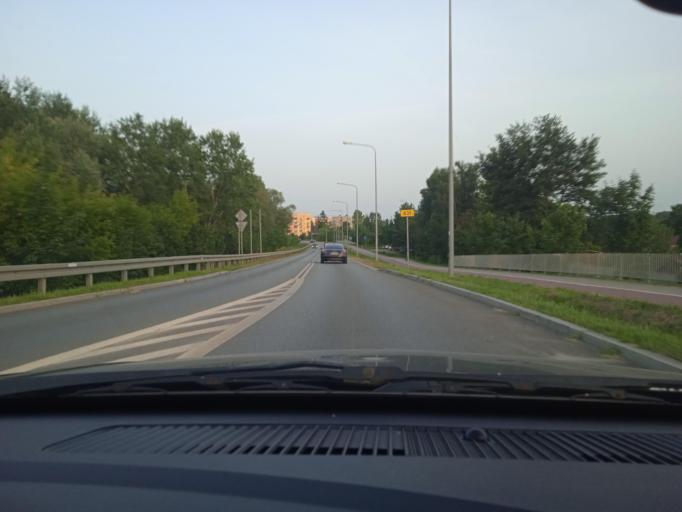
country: PL
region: Masovian Voivodeship
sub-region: Powiat nowodworski
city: Nowy Dwor Mazowiecki
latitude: 52.4310
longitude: 20.7046
